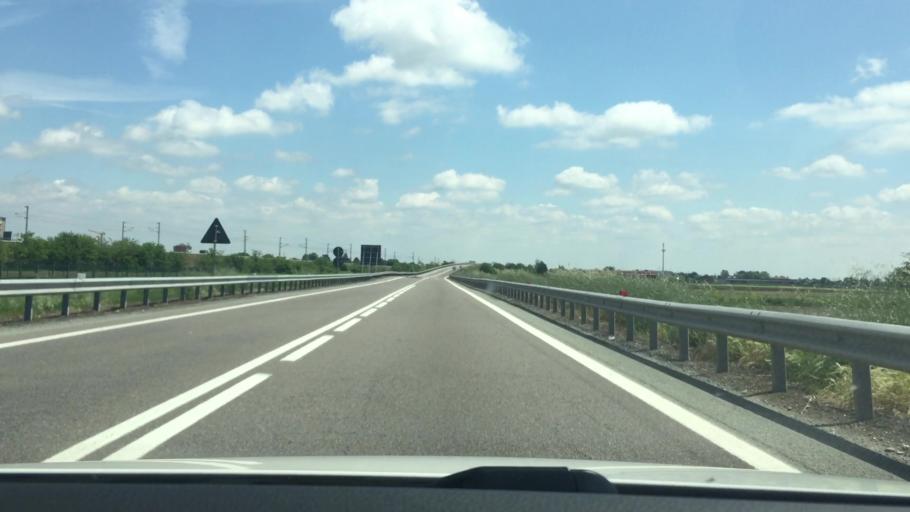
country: IT
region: Piedmont
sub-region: Provincia di Novara
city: Pernate
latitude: 45.4665
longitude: 8.6854
